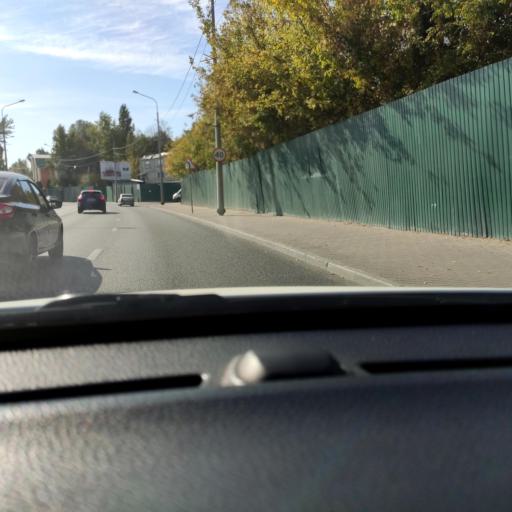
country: RU
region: Voronezj
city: Voronezh
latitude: 51.6860
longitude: 39.2291
